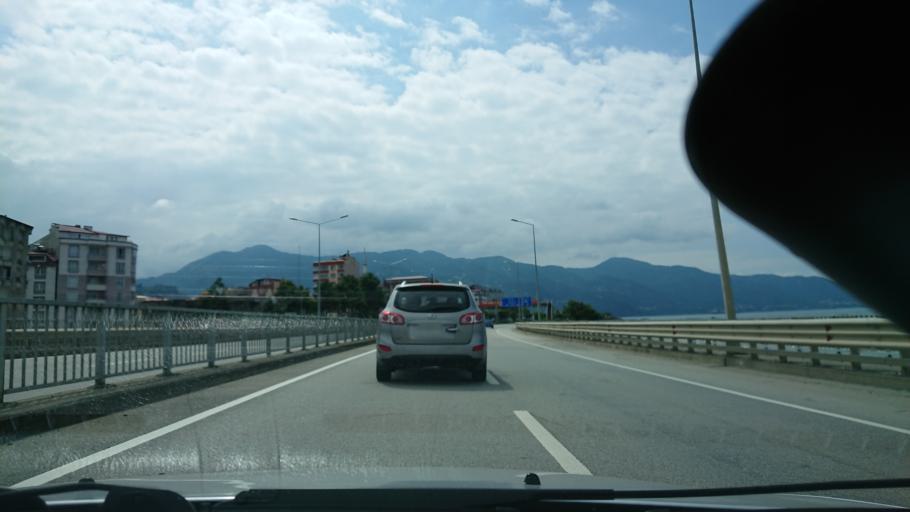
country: TR
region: Trabzon
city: Espiye
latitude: 40.9505
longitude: 38.7148
